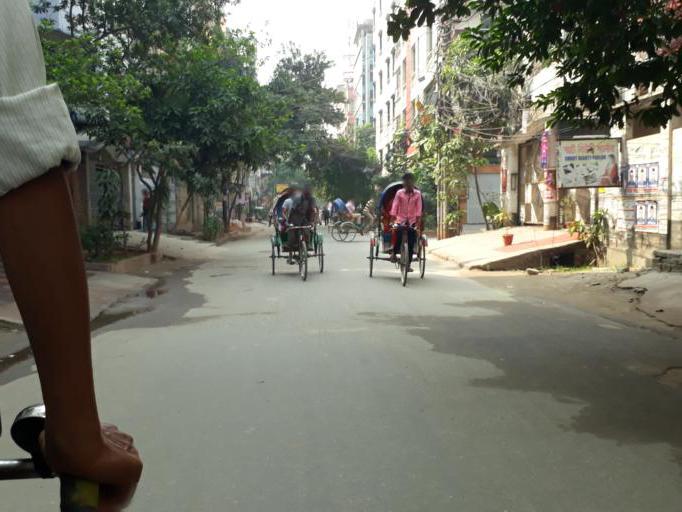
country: BD
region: Dhaka
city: Tungi
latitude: 23.8777
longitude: 90.3901
